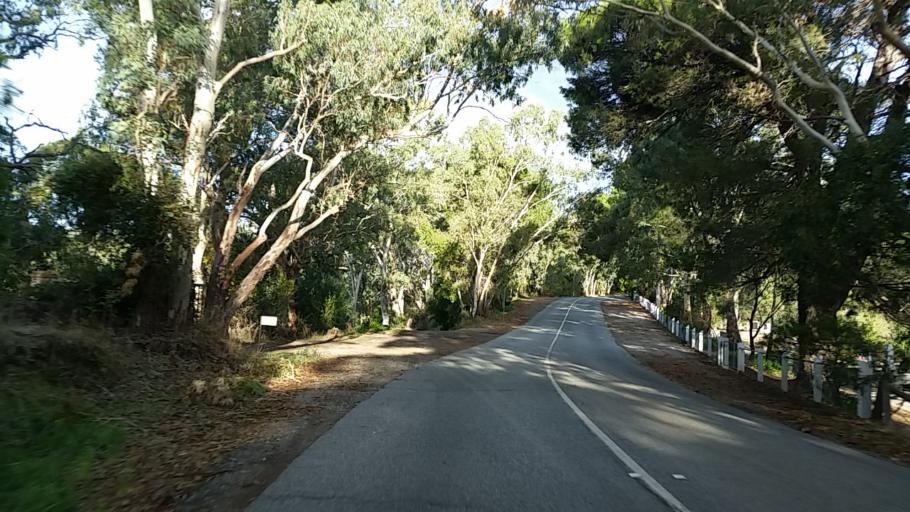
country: AU
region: South Australia
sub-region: Adelaide Hills
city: Adelaide Hills
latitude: -34.8905
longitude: 138.7501
